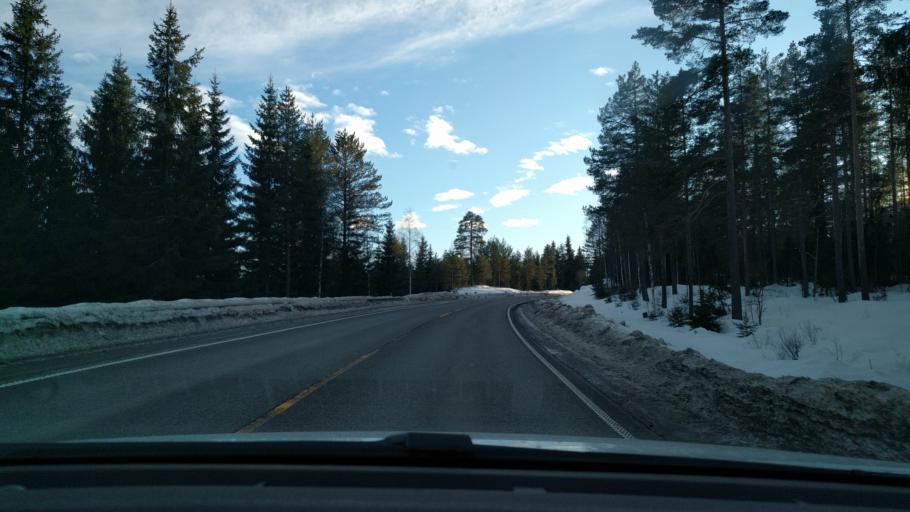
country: NO
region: Hedmark
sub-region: Elverum
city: Elverum
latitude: 61.0203
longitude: 11.8597
